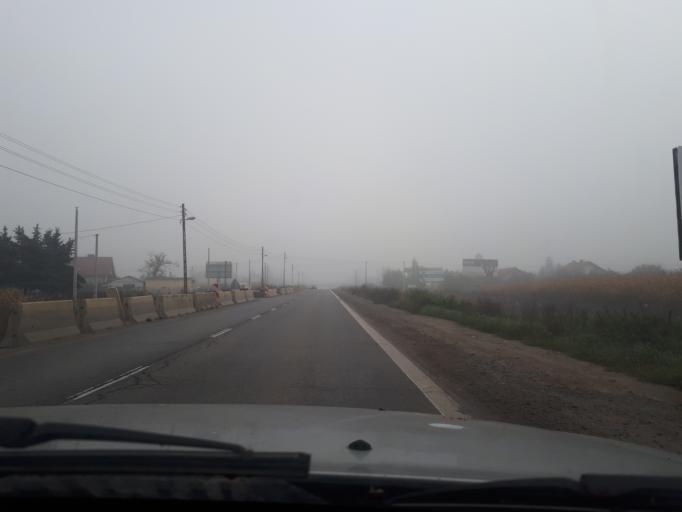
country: PL
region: Lesser Poland Voivodeship
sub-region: Powiat wielicki
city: Podleze
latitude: 50.0780
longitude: 20.1640
